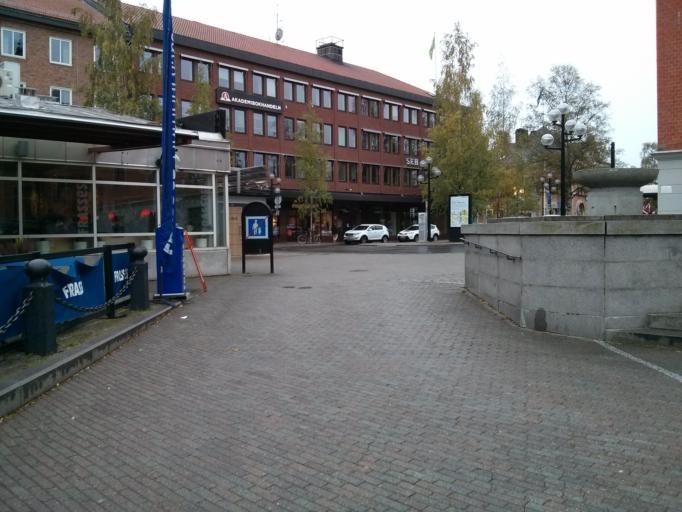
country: SE
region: Vaesterbotten
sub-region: Umea Kommun
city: Umea
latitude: 63.8256
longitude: 20.2634
